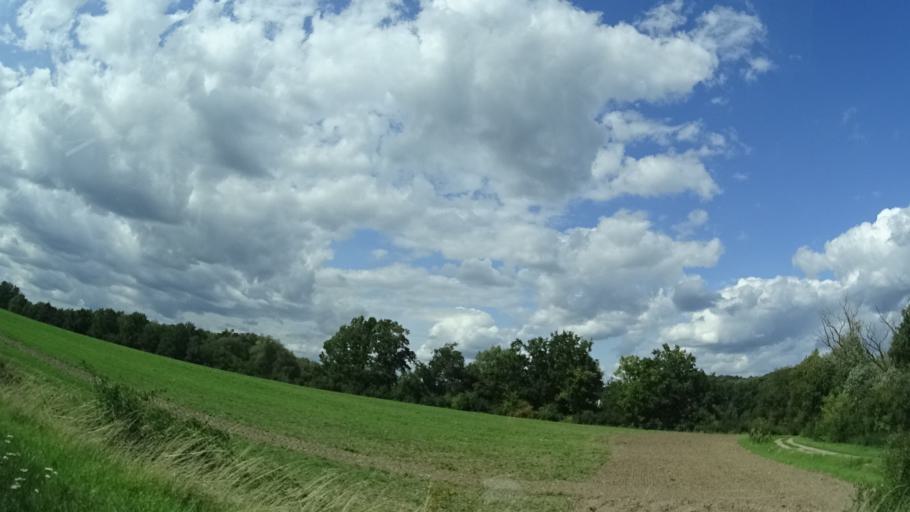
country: DE
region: Bavaria
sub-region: Regierungsbezirk Unterfranken
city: Sand
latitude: 49.9868
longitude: 10.6036
